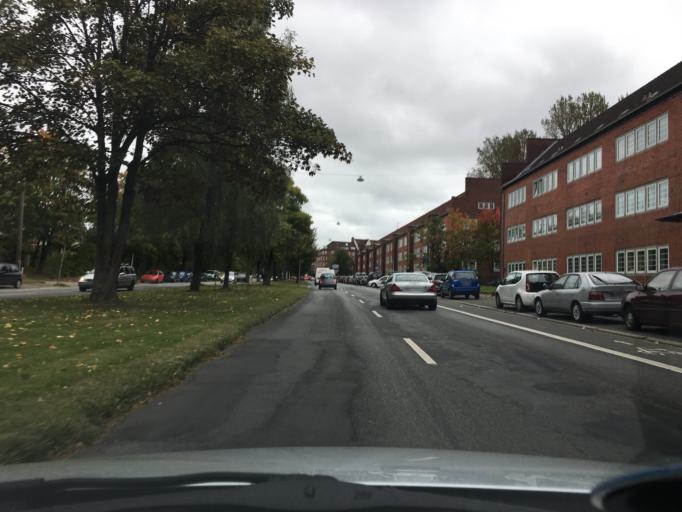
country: DE
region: Schleswig-Holstein
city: Kiel
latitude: 54.3297
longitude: 10.1205
